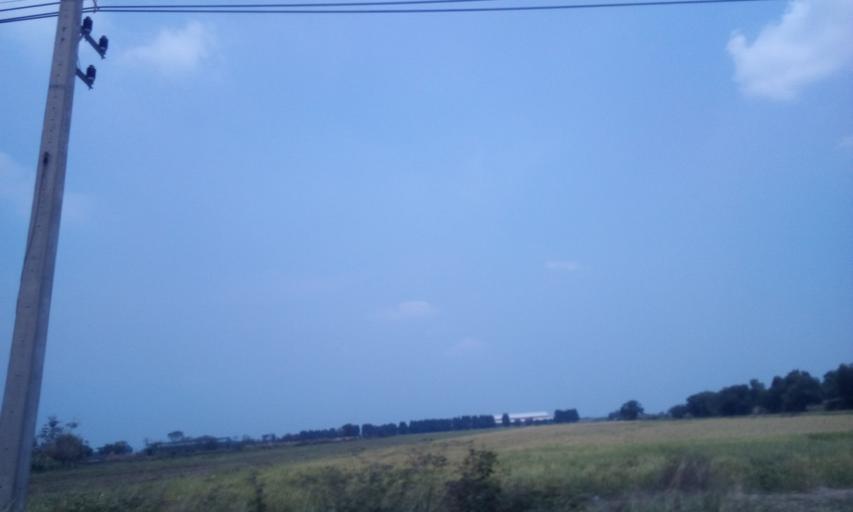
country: TH
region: Bangkok
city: Nong Chok
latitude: 13.9617
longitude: 100.9028
